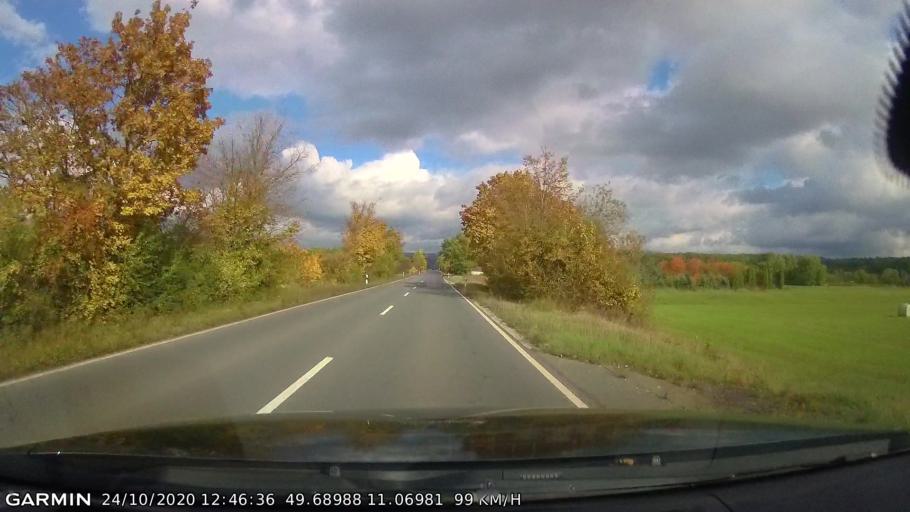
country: DE
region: Bavaria
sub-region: Upper Franconia
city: Poxdorf
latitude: 49.6900
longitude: 11.0699
